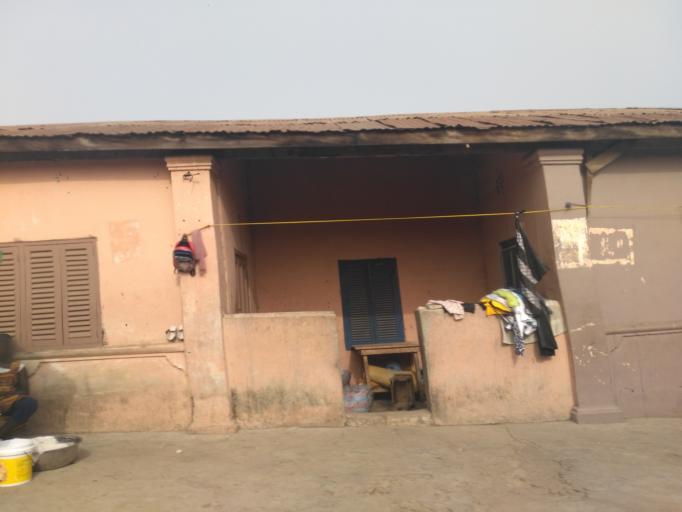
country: GH
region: Ashanti
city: Kumasi
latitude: 6.6864
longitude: -1.6106
